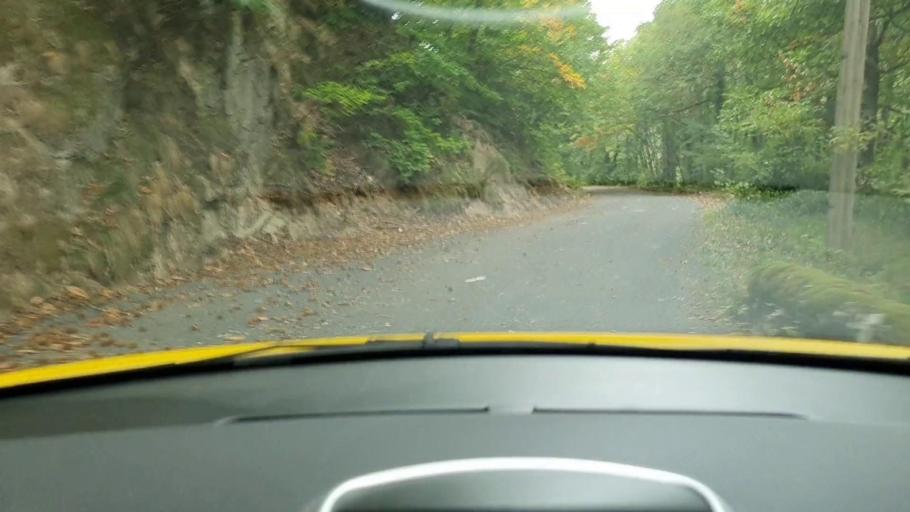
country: FR
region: Languedoc-Roussillon
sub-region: Departement de la Lozere
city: Meyrueis
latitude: 44.0618
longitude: 3.4311
